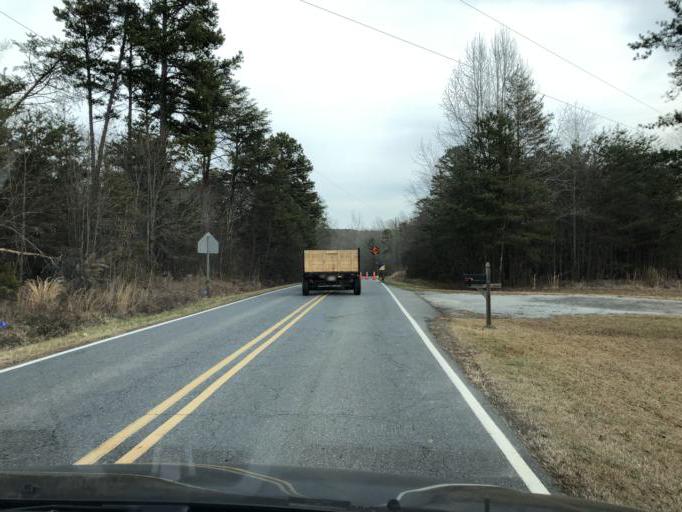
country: US
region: North Carolina
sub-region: Cleveland County
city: Boiling Springs
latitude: 35.2407
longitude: -81.6497
